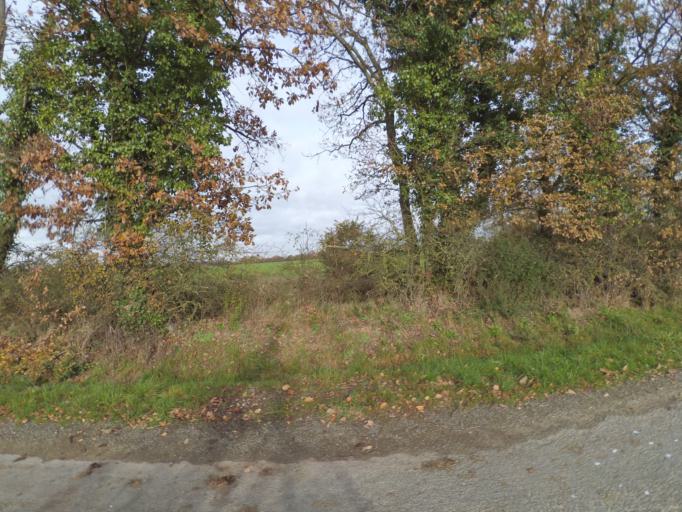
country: FR
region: Pays de la Loire
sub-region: Departement de la Loire-Atlantique
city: La Planche
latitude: 47.0144
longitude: -1.4051
